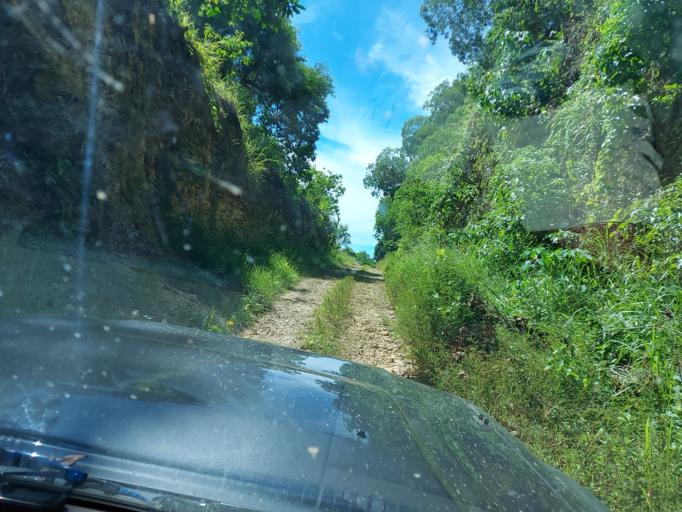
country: VU
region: Malampa
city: Lakatoro
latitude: -16.3280
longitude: 167.7270
